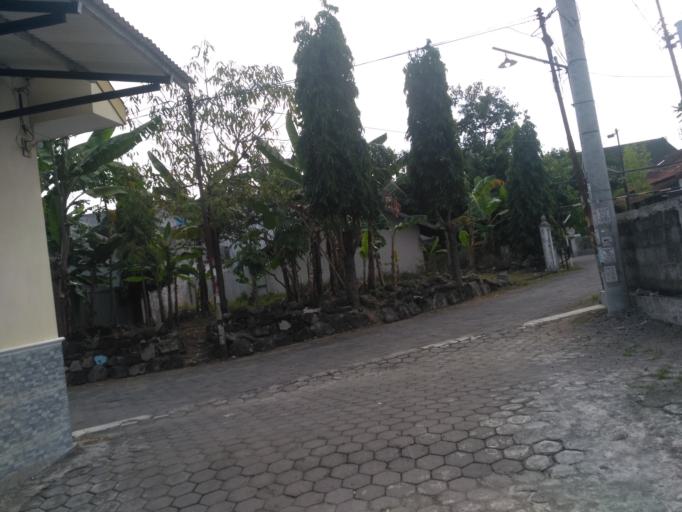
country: ID
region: Daerah Istimewa Yogyakarta
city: Depok
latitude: -7.7675
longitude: 110.4083
